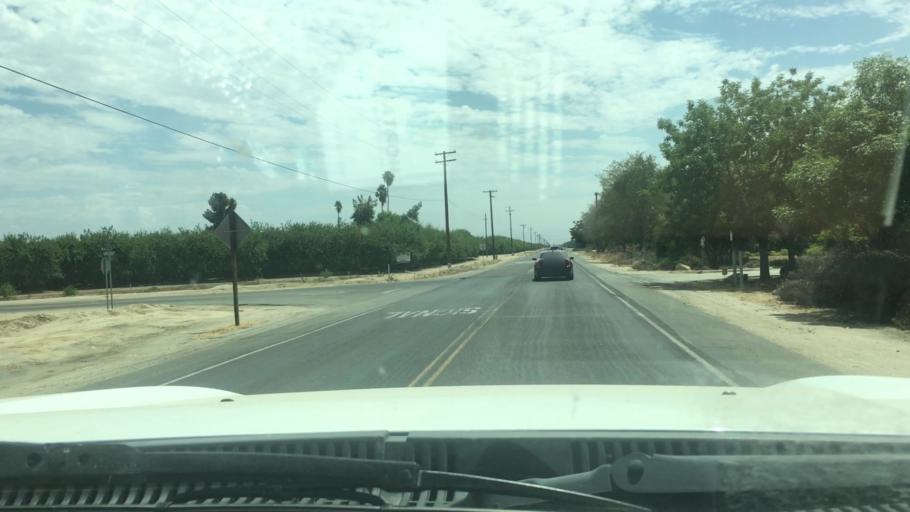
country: US
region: California
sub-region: Kern County
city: Wasco
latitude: 35.5580
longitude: -119.3296
